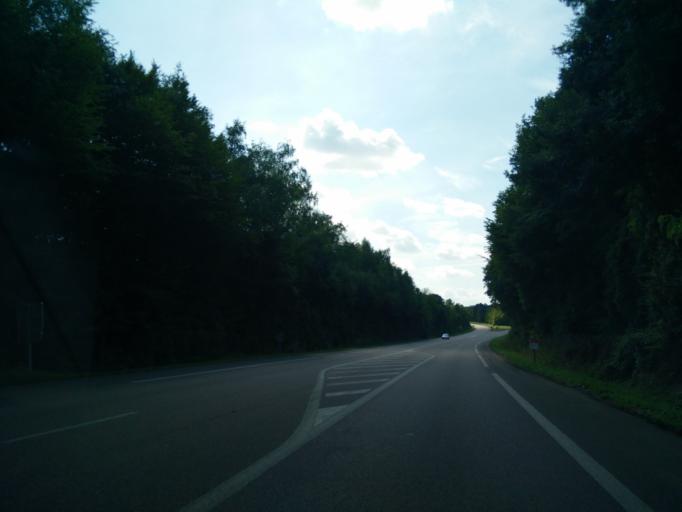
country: FR
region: Ile-de-France
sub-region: Departement des Yvelines
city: Bonnieres-sur-Seine
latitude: 49.0222
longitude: 1.5866
